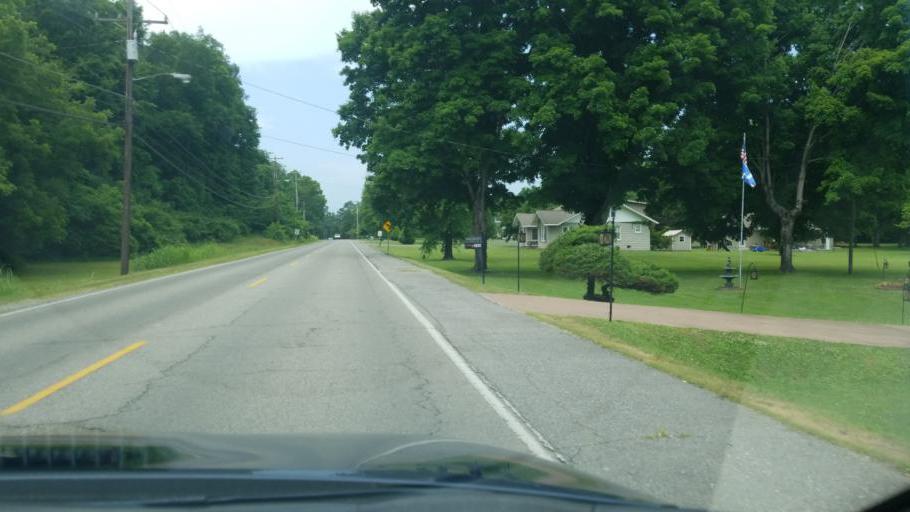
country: US
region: Tennessee
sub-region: Humphreys County
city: Waverly
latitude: 36.0825
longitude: -87.8164
